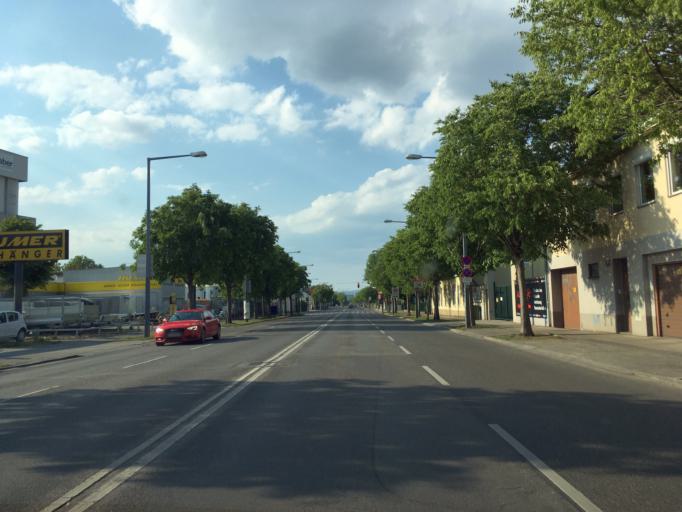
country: AT
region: Lower Austria
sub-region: Politischer Bezirk Modling
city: Vosendorf
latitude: 48.1401
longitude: 16.3242
